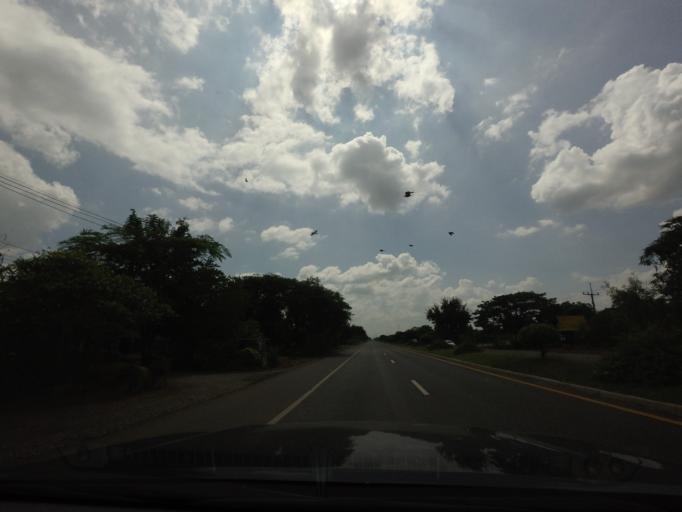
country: TH
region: Phetchabun
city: Nong Phai
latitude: 16.1699
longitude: 101.0770
